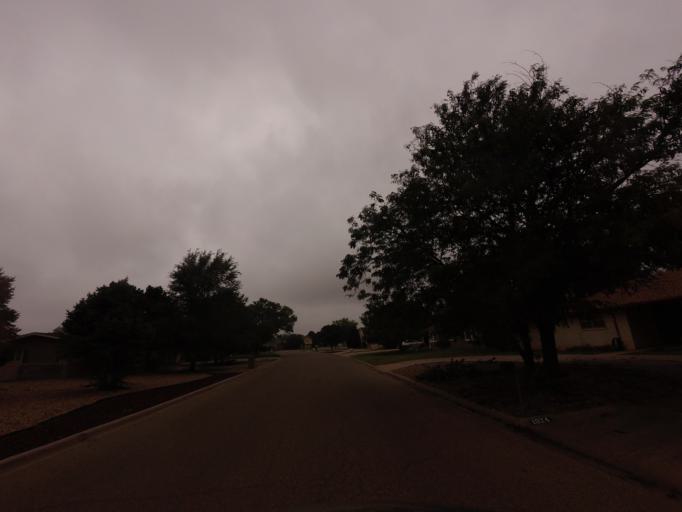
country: US
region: New Mexico
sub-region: Curry County
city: Clovis
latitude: 34.4387
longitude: -103.1921
